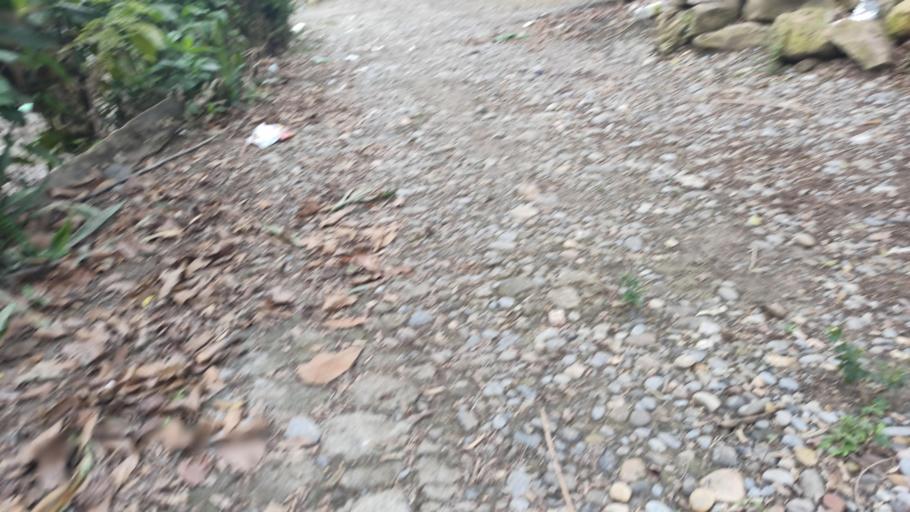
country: MX
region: Veracruz
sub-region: Coatzintla
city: Manuel Maria Contreras
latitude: 20.3613
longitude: -97.5135
